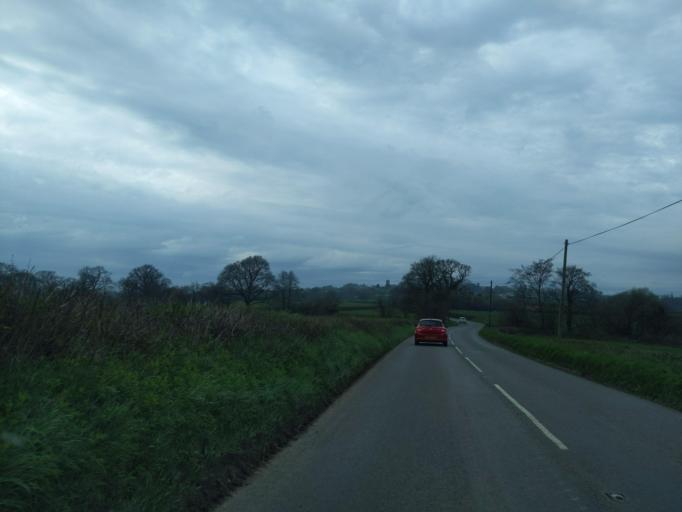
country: GB
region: England
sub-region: Devon
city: Winkleigh
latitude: 50.8494
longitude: -3.9273
